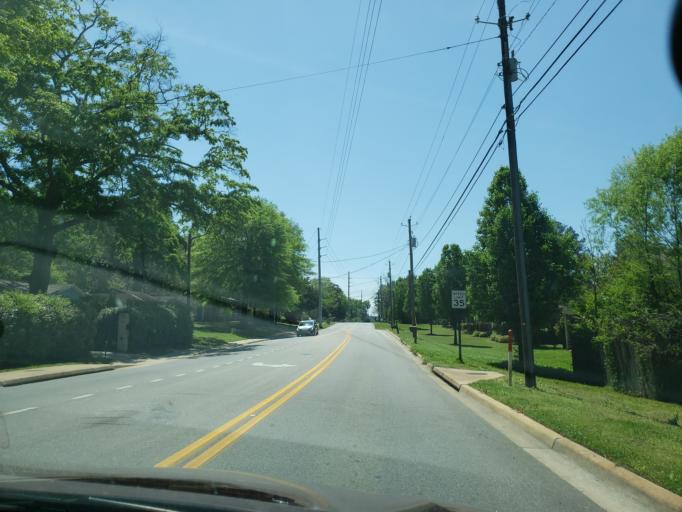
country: US
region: Alabama
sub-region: Lee County
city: Auburn
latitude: 32.6177
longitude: -85.4905
